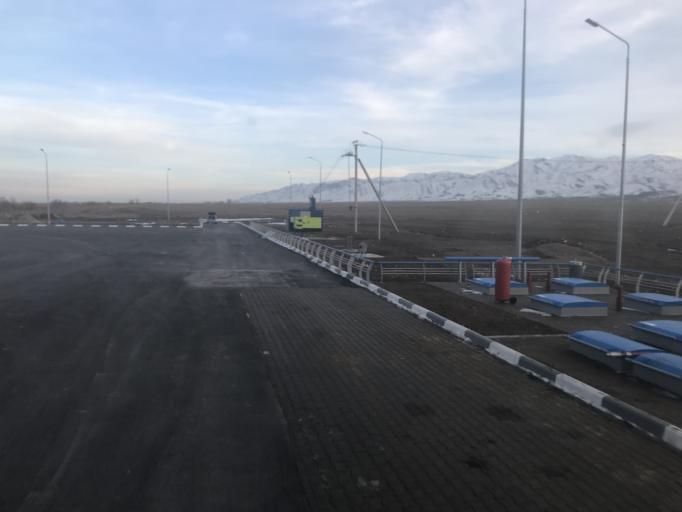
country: KG
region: Chuy
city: Ivanovka
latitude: 43.3988
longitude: 75.1162
